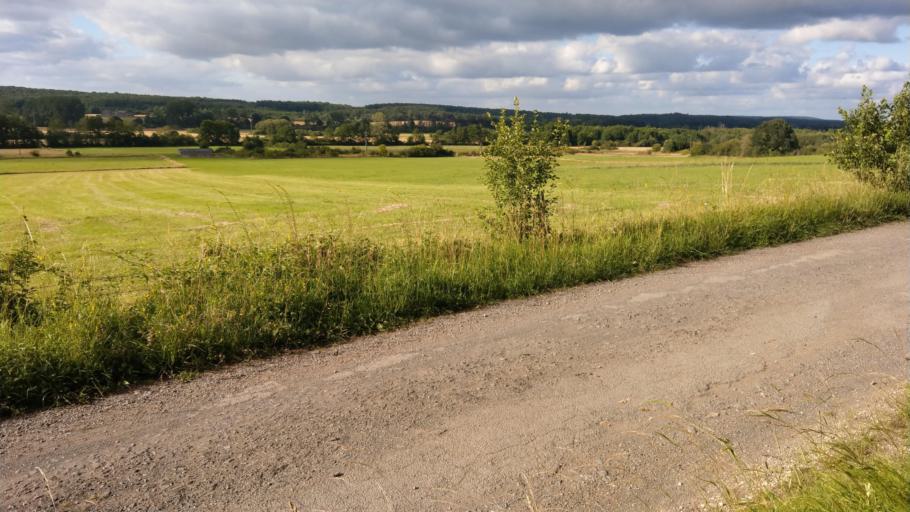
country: BE
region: Wallonia
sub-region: Province de Namur
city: Couvin
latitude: 50.0674
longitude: 4.4361
